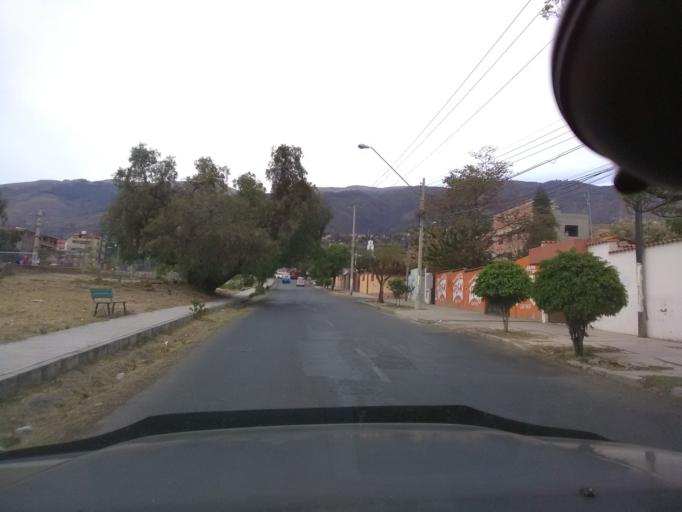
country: BO
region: Cochabamba
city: Cochabamba
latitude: -17.3686
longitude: -66.1492
